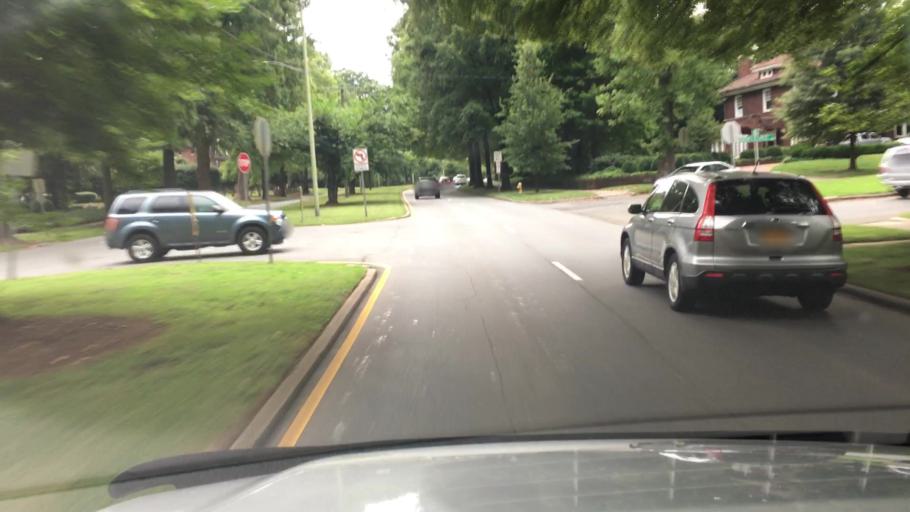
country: US
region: North Carolina
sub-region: Mecklenburg County
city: Charlotte
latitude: 35.2007
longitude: -80.8318
